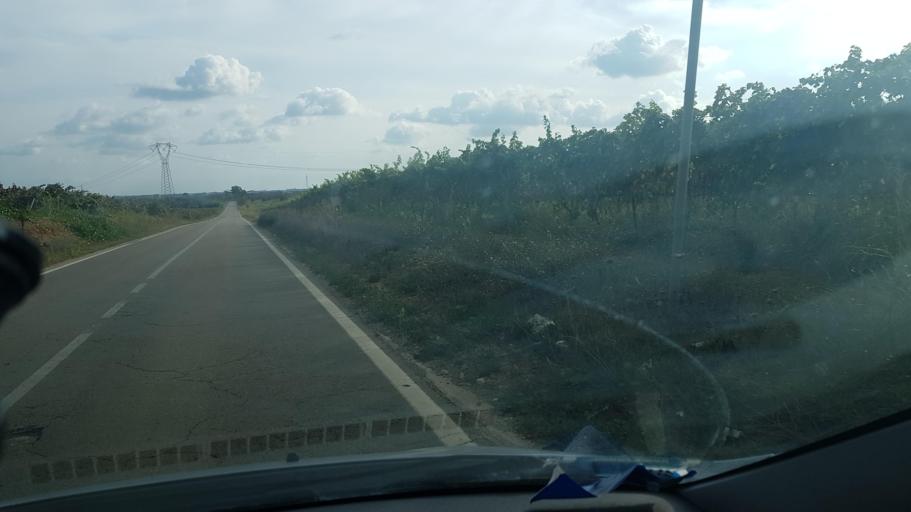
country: IT
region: Apulia
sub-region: Provincia di Brindisi
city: Cellino San Marco
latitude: 40.4565
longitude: 17.9555
